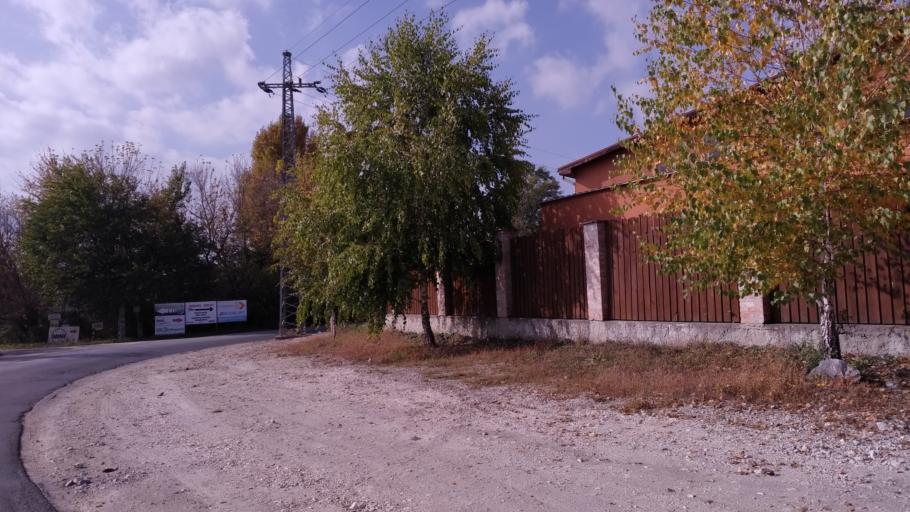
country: HU
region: Pest
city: Pomaz
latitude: 47.6397
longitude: 19.0434
